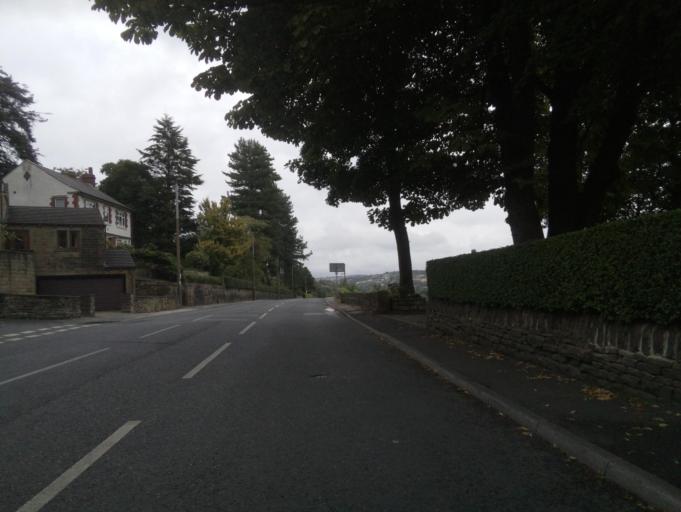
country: GB
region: England
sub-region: Kirklees
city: Holmfirth
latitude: 53.5621
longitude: -1.8083
